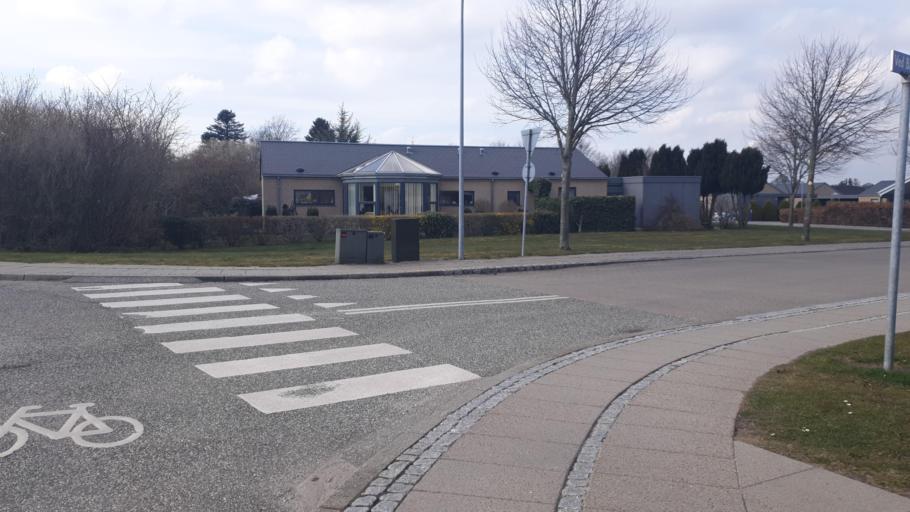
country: DK
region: Central Jutland
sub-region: Hedensted Kommune
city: Hedensted
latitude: 55.7661
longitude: 9.7113
